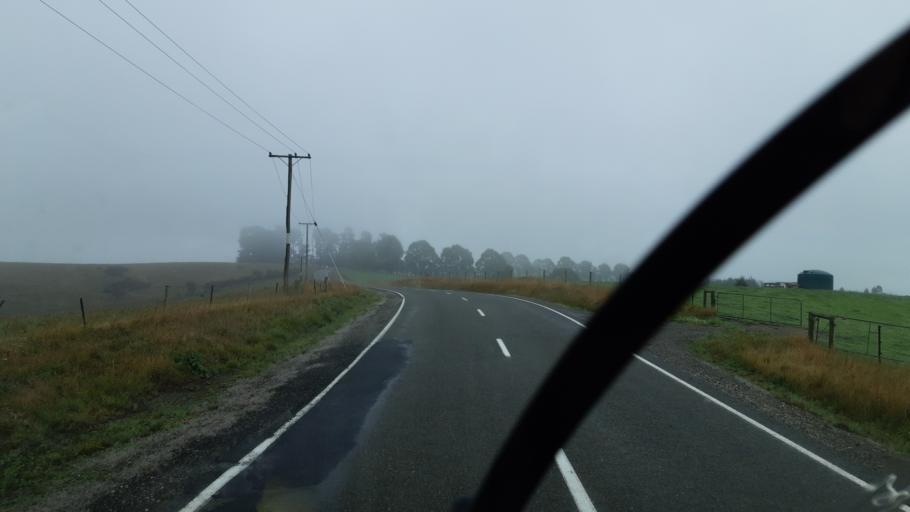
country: NZ
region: Otago
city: Oamaru
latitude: -44.9355
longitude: 170.7717
